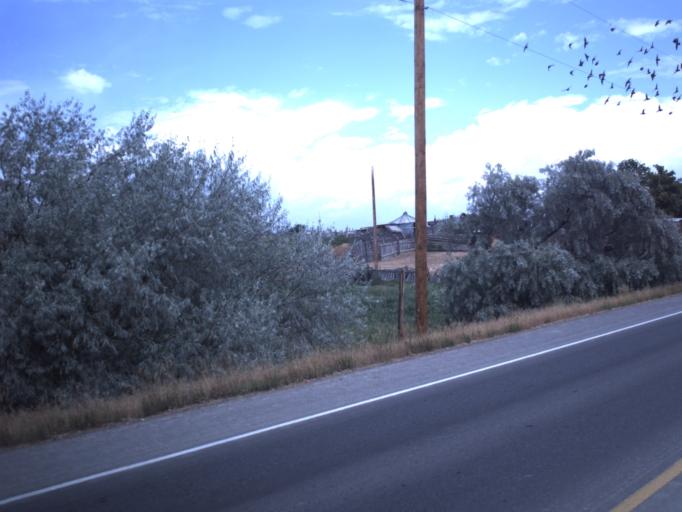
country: US
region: Utah
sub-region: Uintah County
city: Naples
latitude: 40.3757
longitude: -109.4984
